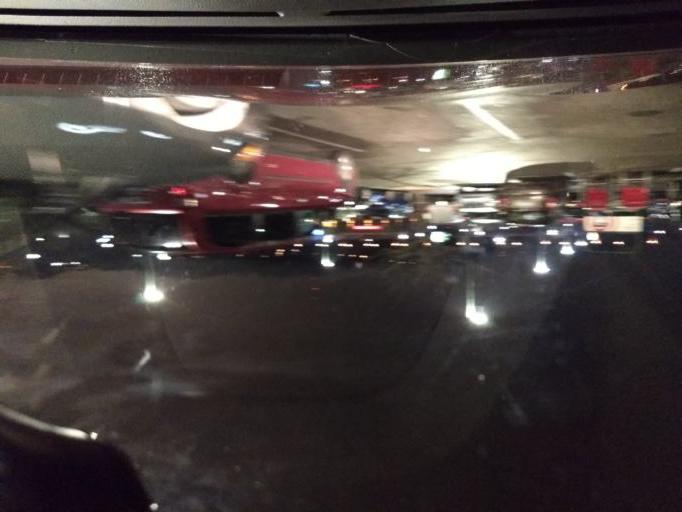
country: US
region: Pennsylvania
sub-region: Allegheny County
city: Homestead
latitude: 40.4112
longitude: -79.9107
